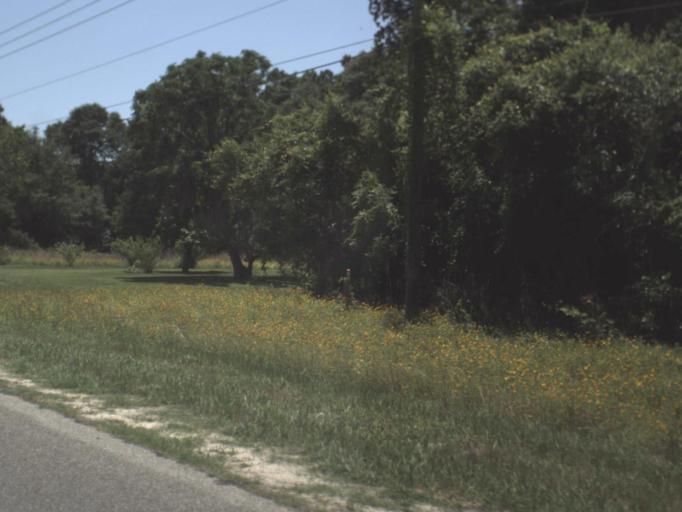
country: US
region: Florida
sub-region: Suwannee County
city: Live Oak
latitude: 30.2581
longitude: -82.9058
